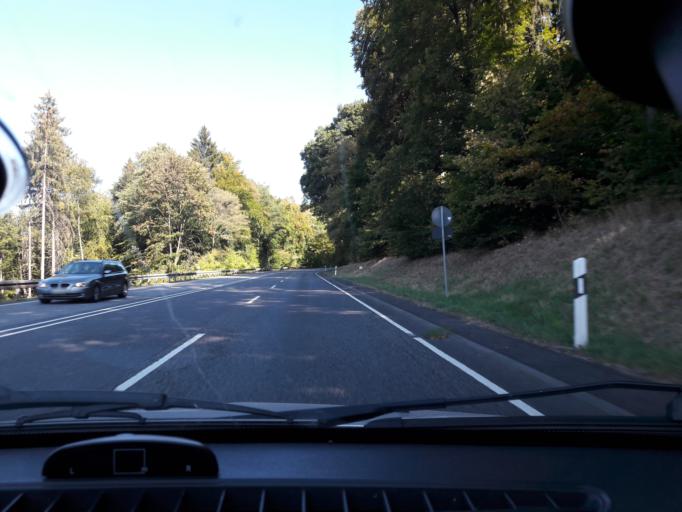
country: DE
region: Hesse
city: Taunusstein
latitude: 50.1149
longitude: 8.1791
